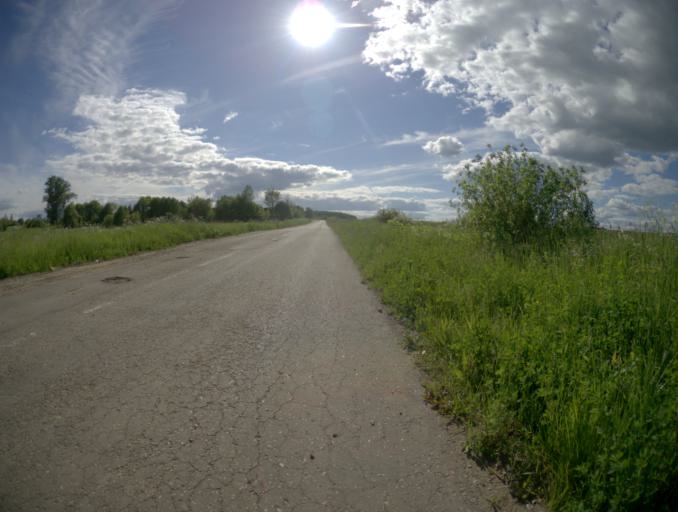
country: RU
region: Ivanovo
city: Kitovo
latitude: 56.8311
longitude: 41.3292
